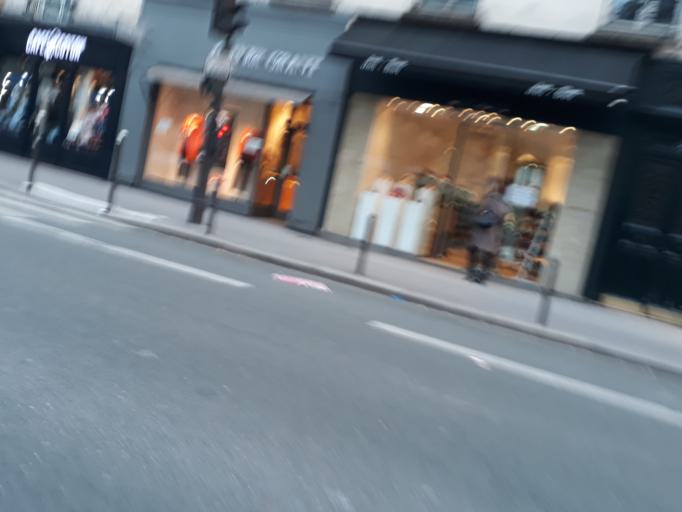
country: FR
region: Ile-de-France
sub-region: Paris
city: Paris
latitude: 48.8520
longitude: 2.3287
